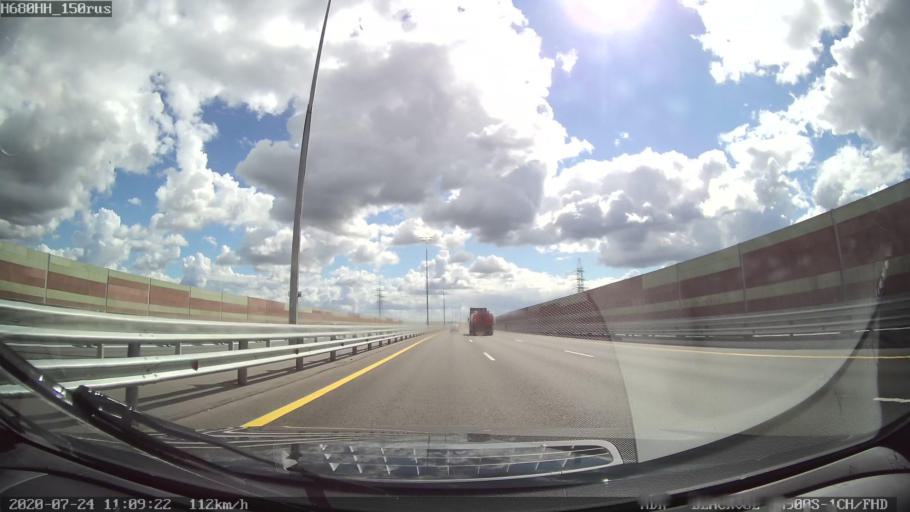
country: RU
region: St.-Petersburg
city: Tyarlevo
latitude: 59.7494
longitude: 30.4732
